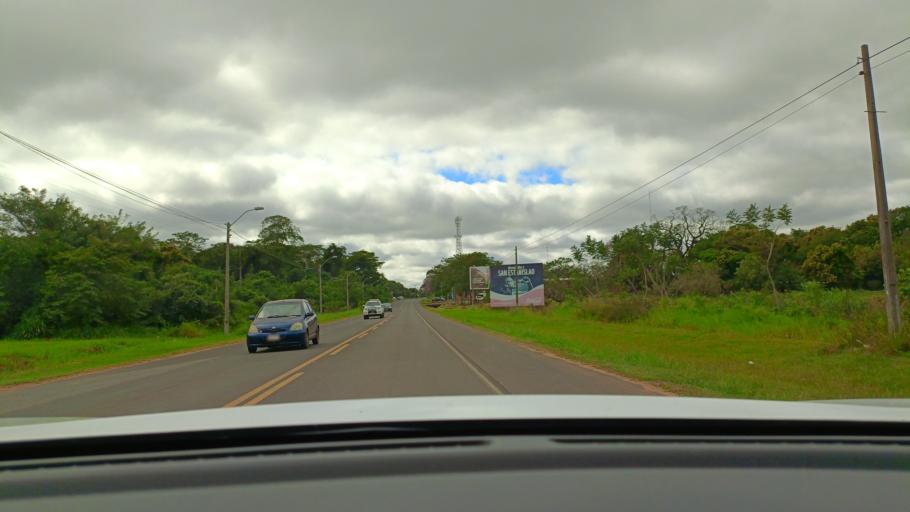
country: PY
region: San Pedro
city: Union
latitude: -24.6815
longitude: -56.4670
